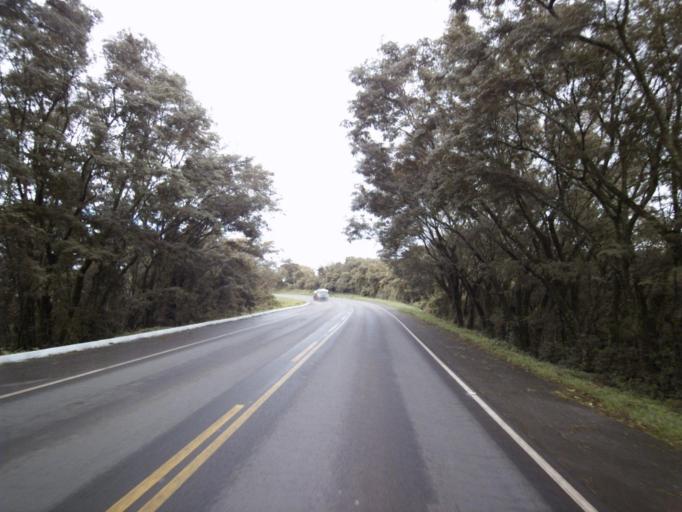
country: BR
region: Santa Catarina
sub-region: Concordia
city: Concordia
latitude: -27.0627
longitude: -51.8924
